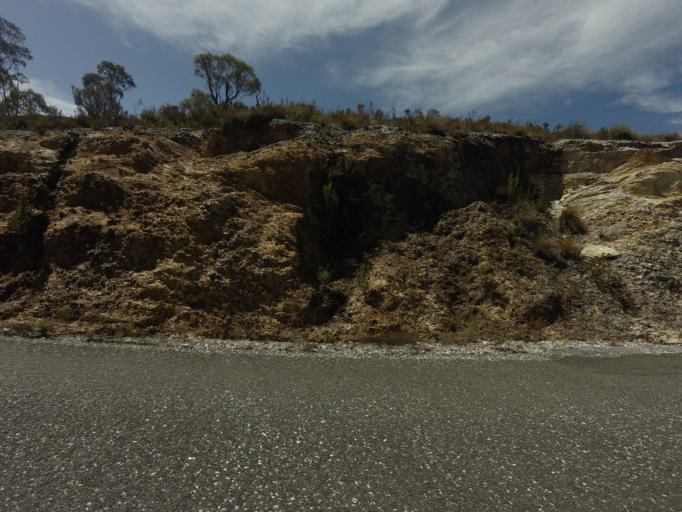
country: AU
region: Tasmania
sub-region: West Coast
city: Queenstown
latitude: -42.7913
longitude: 146.0632
